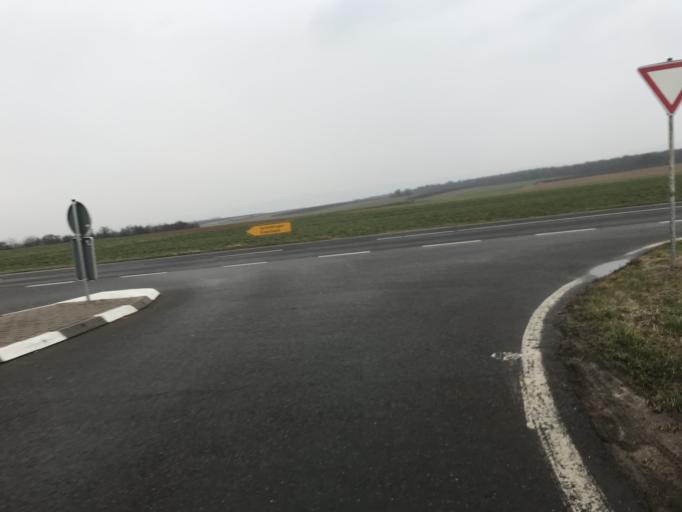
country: DE
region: Rheinland-Pfalz
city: Ober-Olm
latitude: 49.9428
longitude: 8.1752
